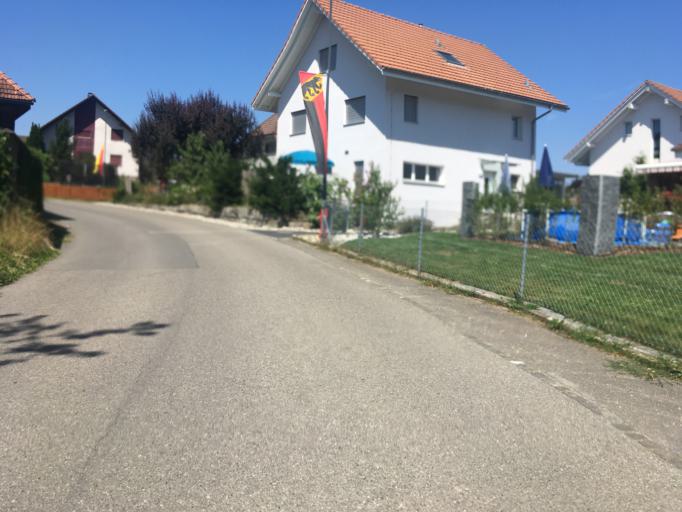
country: CH
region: Solothurn
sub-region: Bezirk Bucheggberg
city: Messen
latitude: 47.0856
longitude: 7.4804
